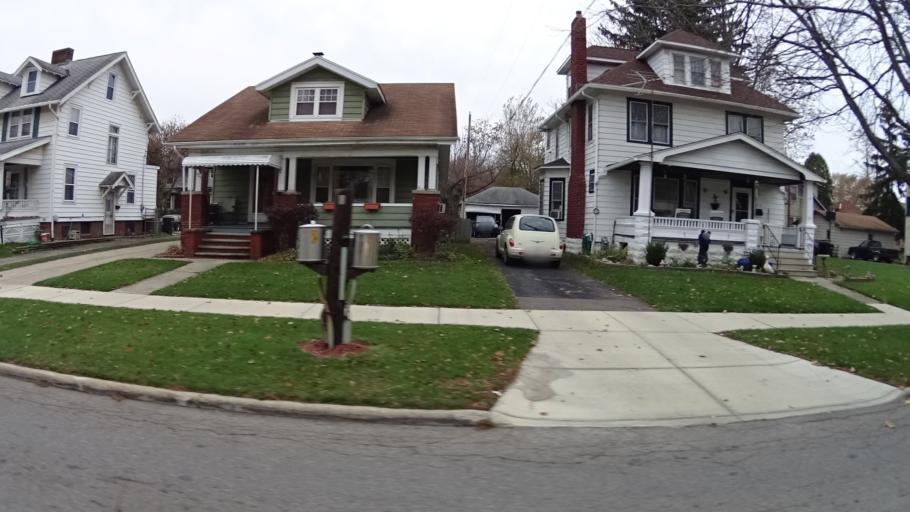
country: US
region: Ohio
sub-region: Lorain County
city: Elyria
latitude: 41.3579
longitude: -82.1105
